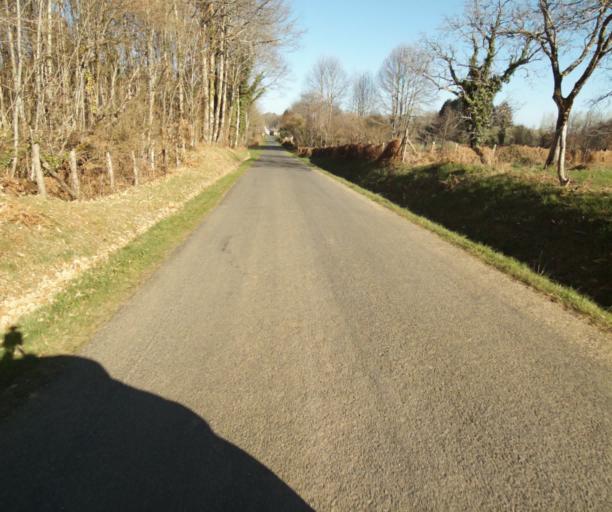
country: FR
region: Limousin
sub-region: Departement de la Correze
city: Saint-Clement
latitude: 45.3735
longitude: 1.6460
